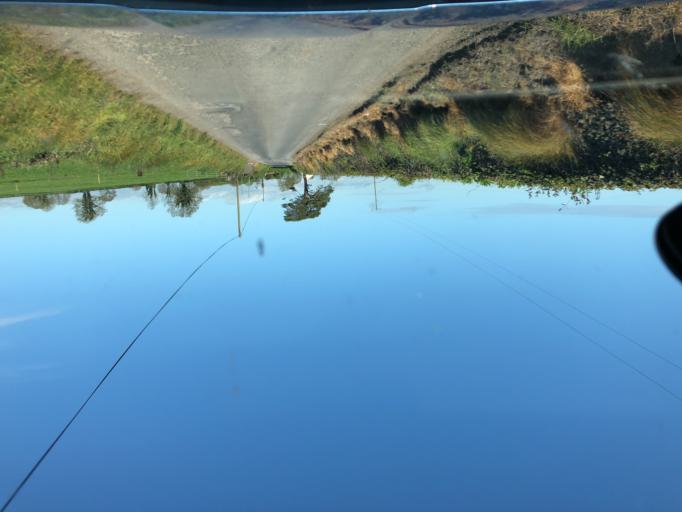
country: IE
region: Connaught
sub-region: County Galway
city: Portumna
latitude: 53.1565
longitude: -8.3179
